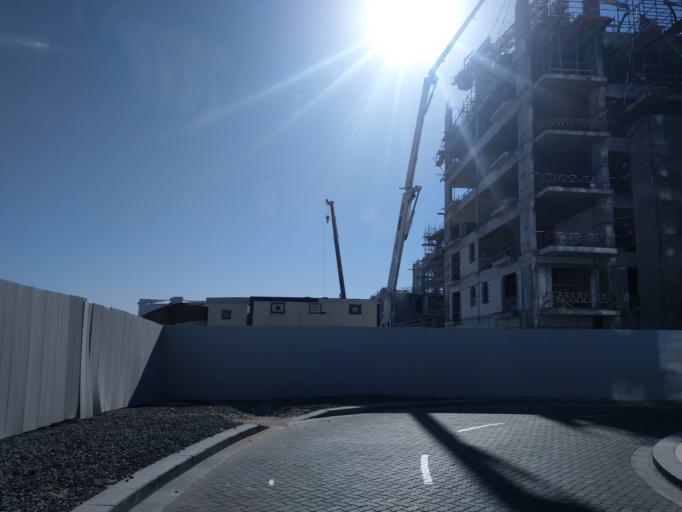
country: AE
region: Abu Dhabi
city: Abu Dhabi
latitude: 24.5209
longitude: 54.4381
